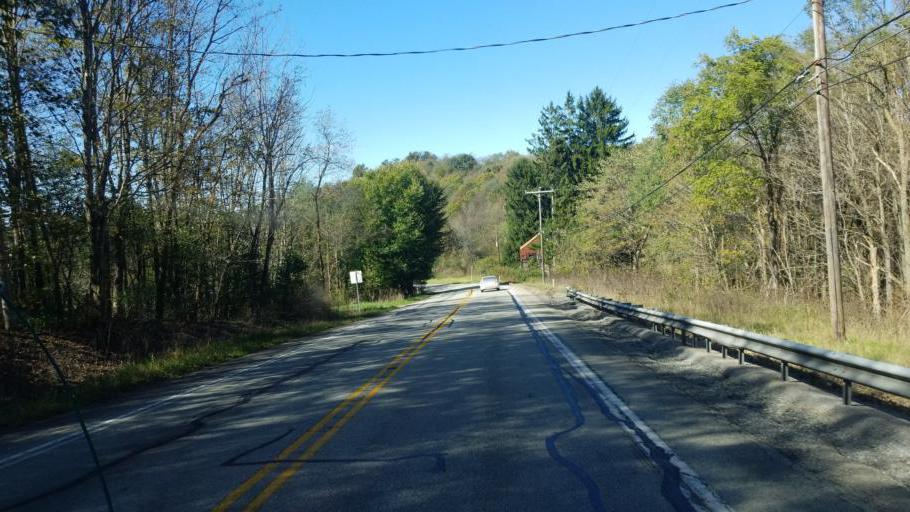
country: US
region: Pennsylvania
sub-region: Somerset County
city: Boswell
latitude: 40.1214
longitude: -78.9722
